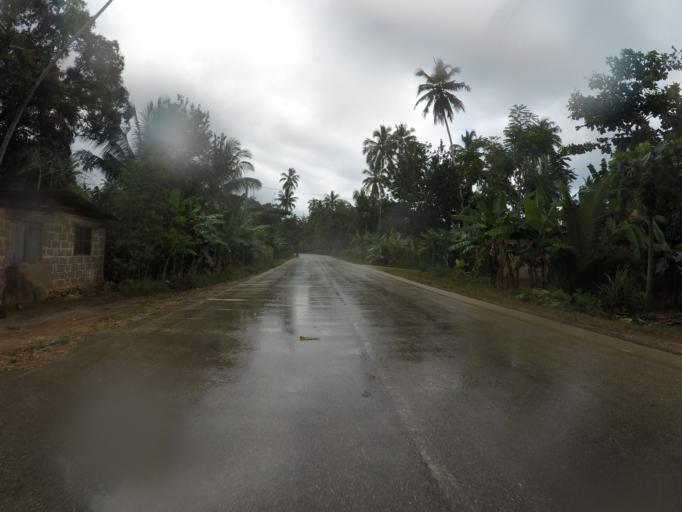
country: TZ
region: Zanzibar North
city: Mkokotoni
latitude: -5.9622
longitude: 39.1948
